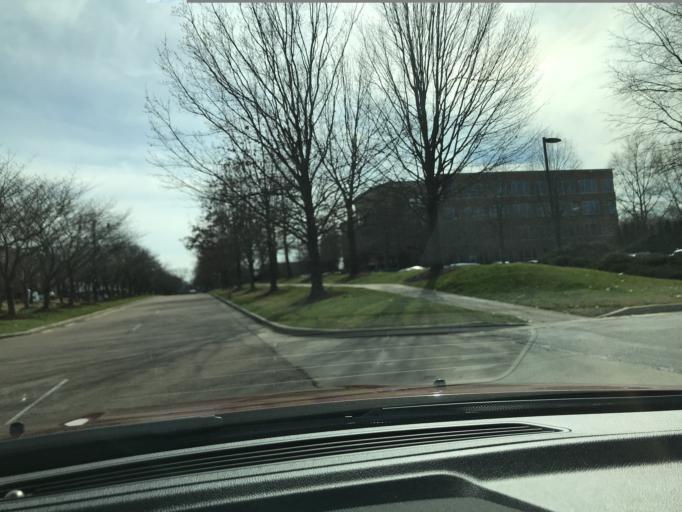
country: US
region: Tennessee
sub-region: Shelby County
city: Collierville
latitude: 35.0414
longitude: -89.7033
